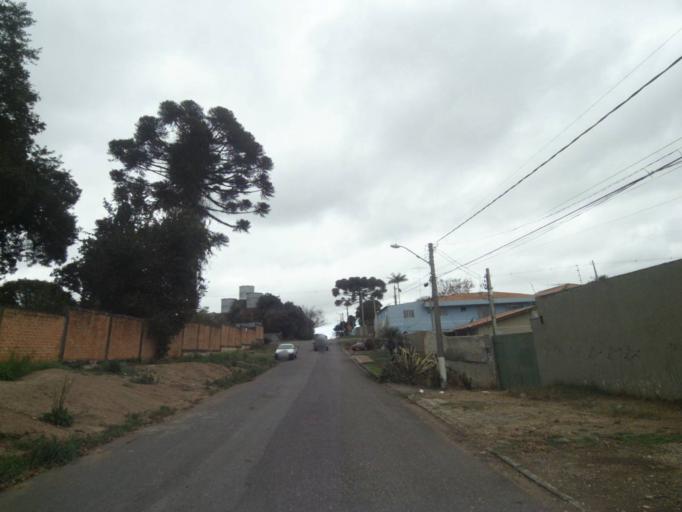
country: BR
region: Parana
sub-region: Sao Jose Dos Pinhais
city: Sao Jose dos Pinhais
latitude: -25.5393
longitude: -49.2993
